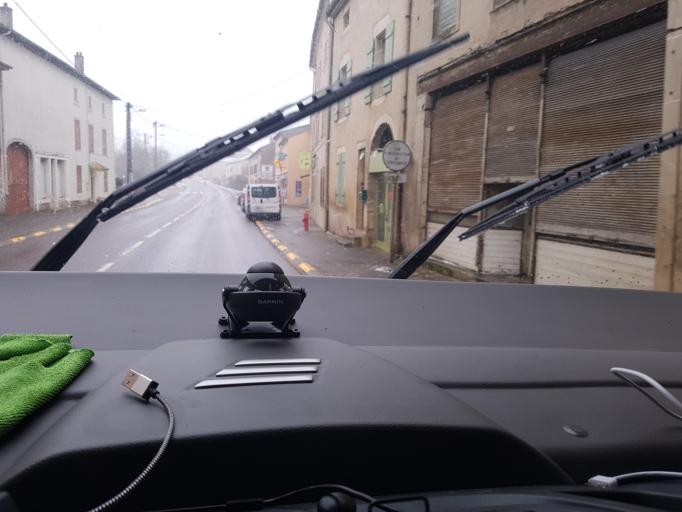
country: FR
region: Lorraine
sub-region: Departement de la Moselle
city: Solgne
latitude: 48.8861
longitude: 6.3932
